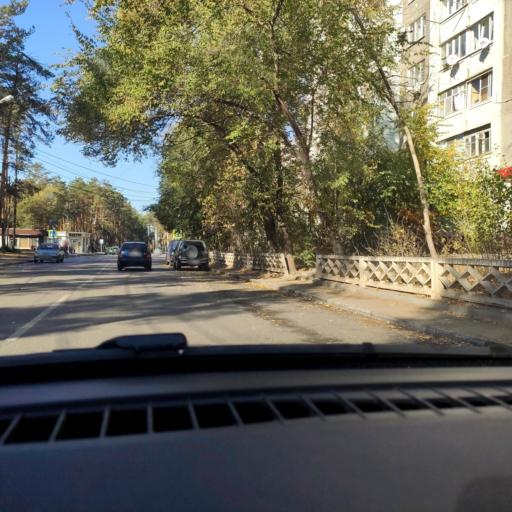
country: RU
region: Voronezj
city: Pridonskoy
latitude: 51.6835
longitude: 39.0836
